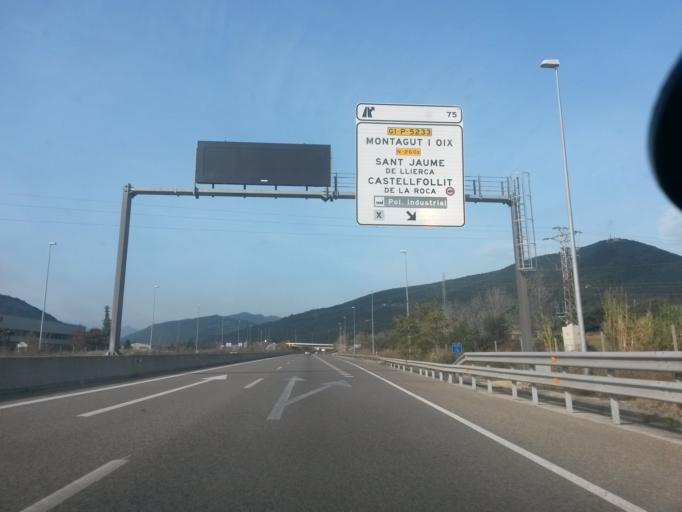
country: ES
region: Catalonia
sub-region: Provincia de Girona
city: Argelaguer
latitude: 42.2185
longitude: 2.5876
